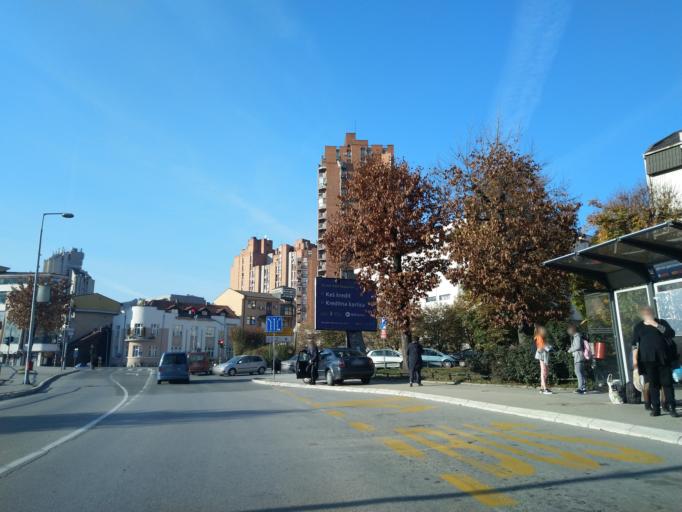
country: RS
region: Central Serbia
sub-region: Zlatiborski Okrug
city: Uzice
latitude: 43.8542
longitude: 19.8431
